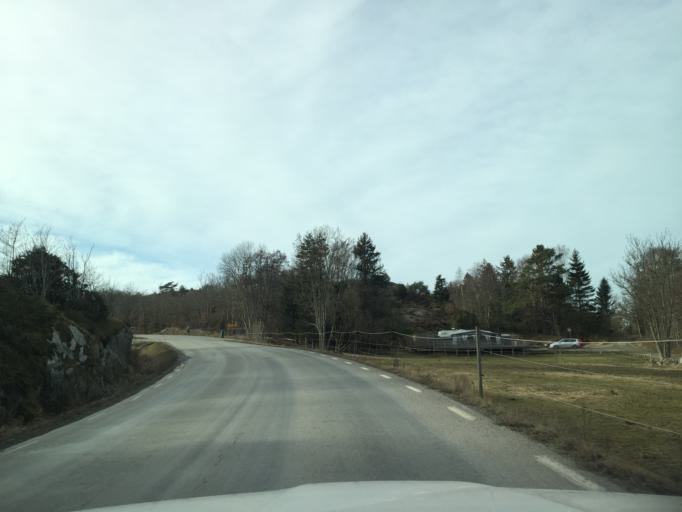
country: SE
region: Vaestra Goetaland
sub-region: Tjorns Kommun
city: Skaerhamn
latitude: 58.0362
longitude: 11.5627
